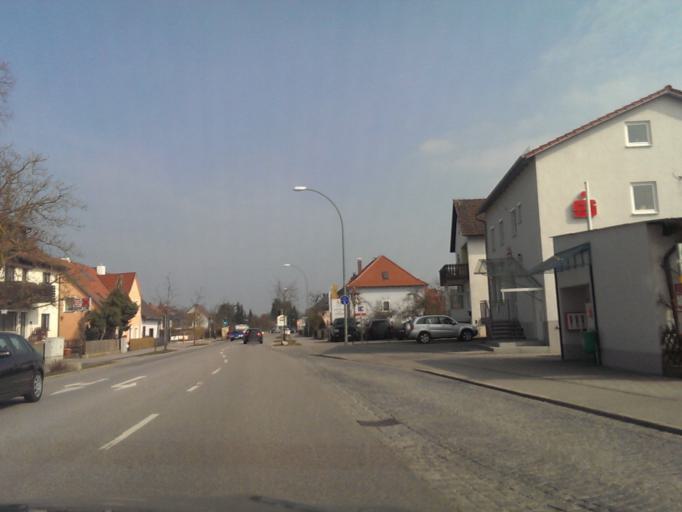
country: DE
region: Bavaria
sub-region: Upper Palatinate
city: Tegernheim
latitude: 49.0247
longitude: 12.1724
